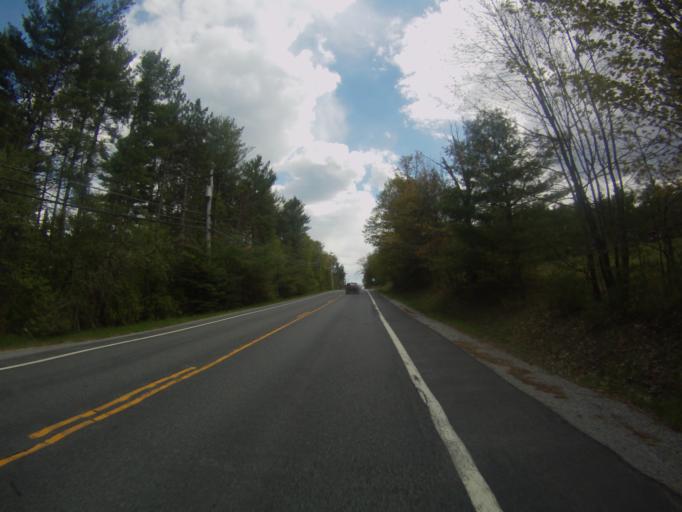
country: US
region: New York
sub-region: Essex County
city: Ticonderoga
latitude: 43.8602
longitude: -73.7554
